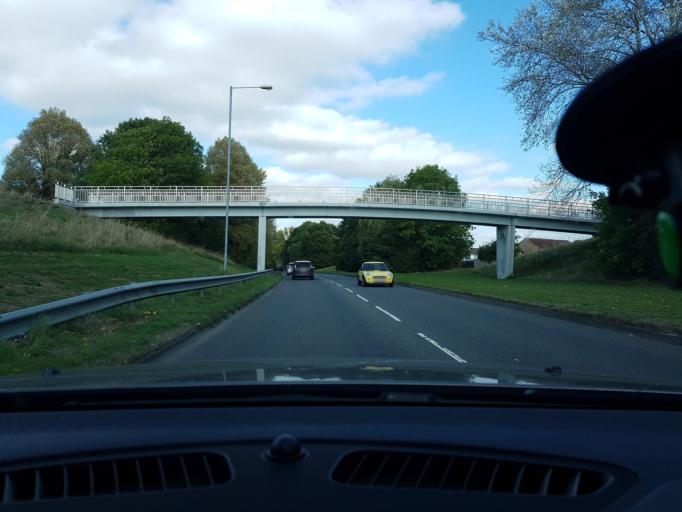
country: GB
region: England
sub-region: Borough of Swindon
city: Chiseldon
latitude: 51.5507
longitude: -1.7341
